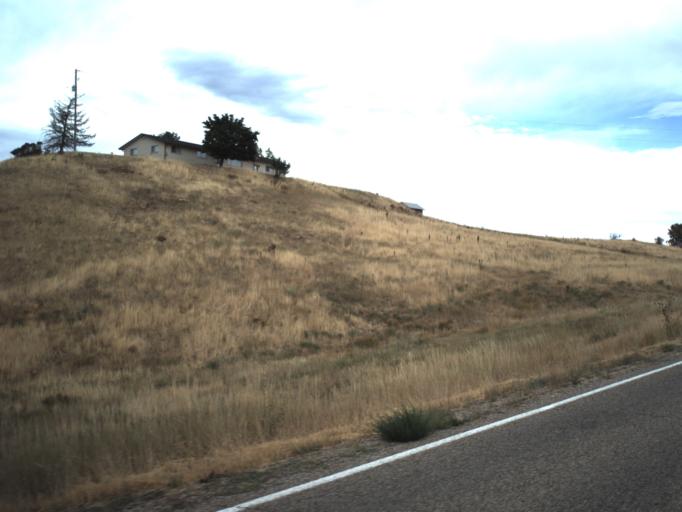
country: US
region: Utah
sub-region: Morgan County
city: Morgan
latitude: 40.9896
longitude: -111.6796
